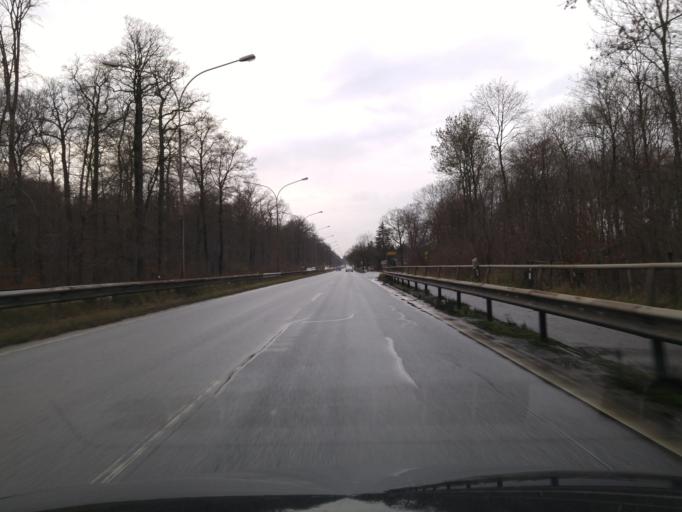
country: DE
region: Schleswig-Holstein
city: Bad Schwartau
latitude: 53.8928
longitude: 10.7344
